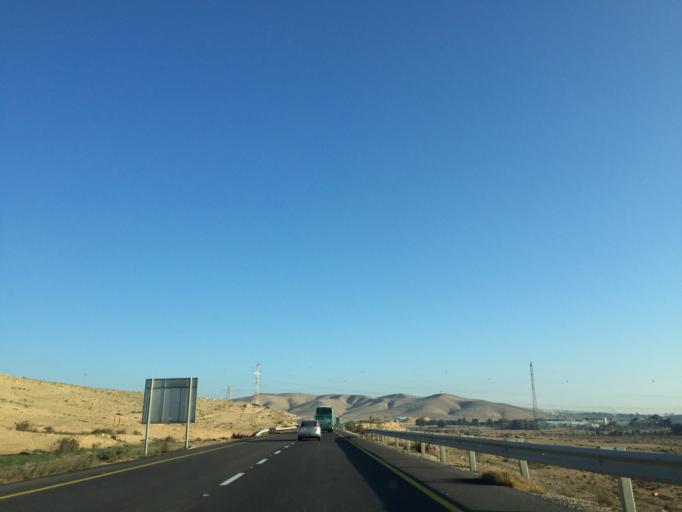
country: IL
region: Southern District
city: Dimona
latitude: 31.0585
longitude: 35.0005
